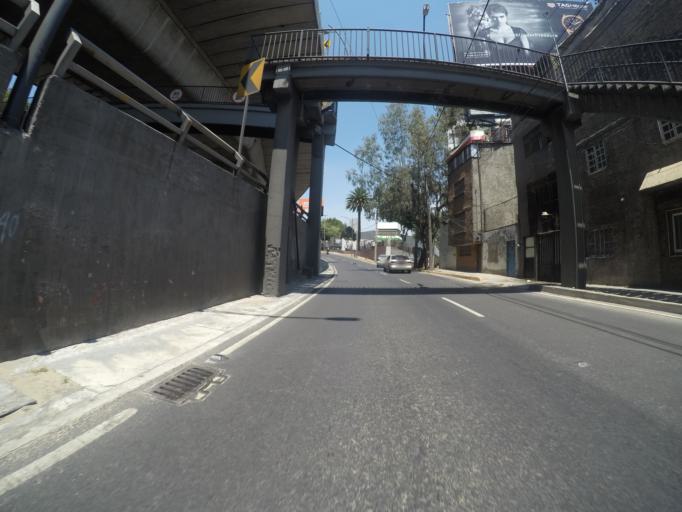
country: MX
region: Mexico City
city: Colonia del Valle
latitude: 19.3920
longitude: -99.1875
